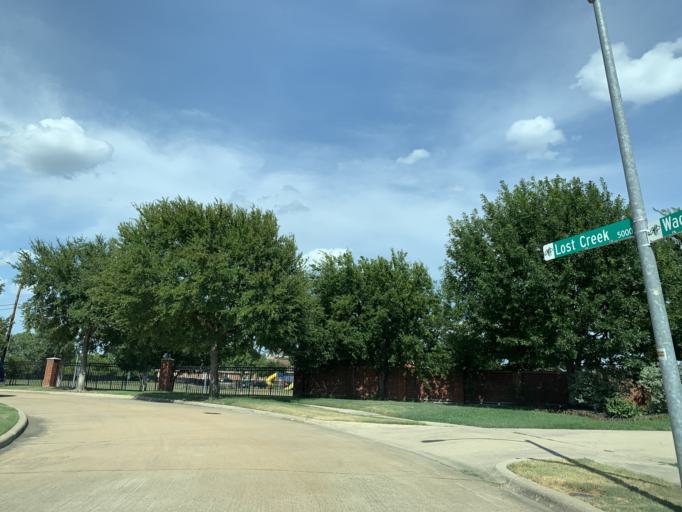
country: US
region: Texas
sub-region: Dallas County
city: Cedar Hill
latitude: 32.6504
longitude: -97.0078
